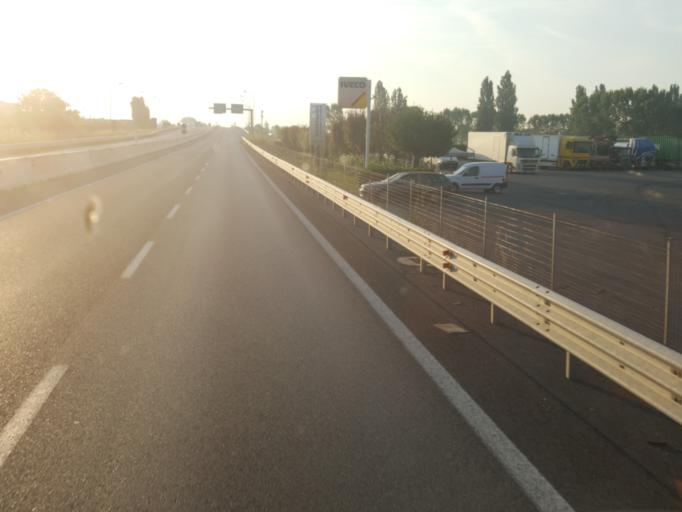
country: IT
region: Lombardy
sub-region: Provincia di Cremona
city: Vaiano Cremasco
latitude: 45.3802
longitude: 9.5838
